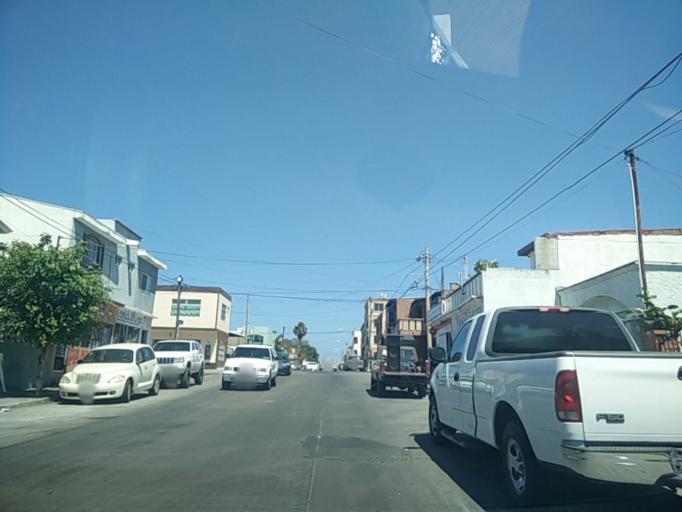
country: MX
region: Baja California
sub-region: Tijuana
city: La Esperanza [Granjas Familiares]
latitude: 32.5113
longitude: -117.1161
